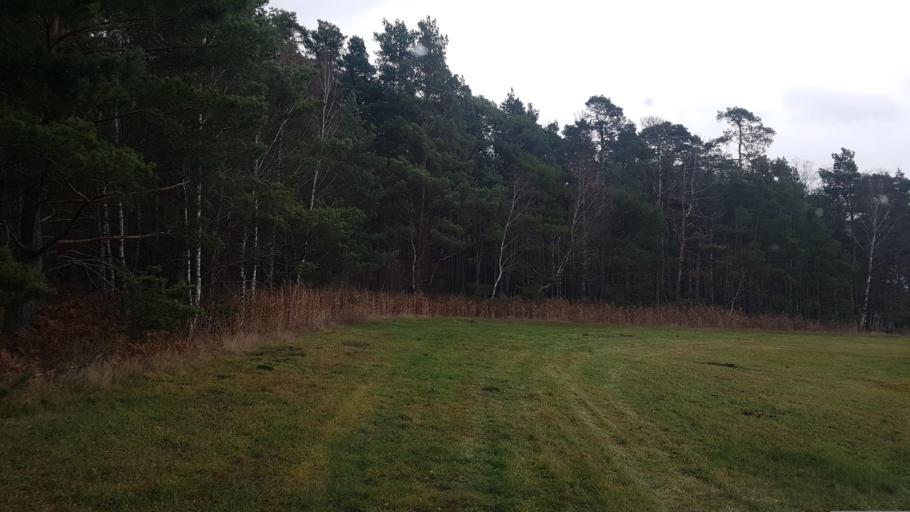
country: DE
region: Brandenburg
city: Ruckersdorf
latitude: 51.5622
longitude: 13.6057
